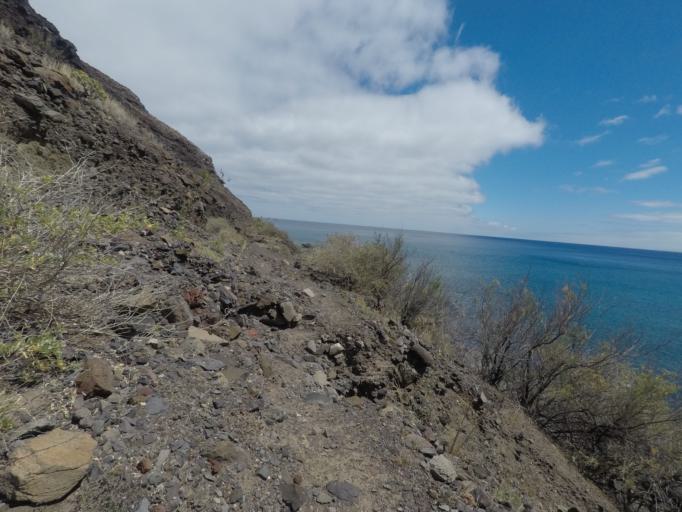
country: PT
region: Madeira
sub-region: Porto Santo
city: Vila de Porto Santo
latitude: 33.0614
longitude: -16.3014
